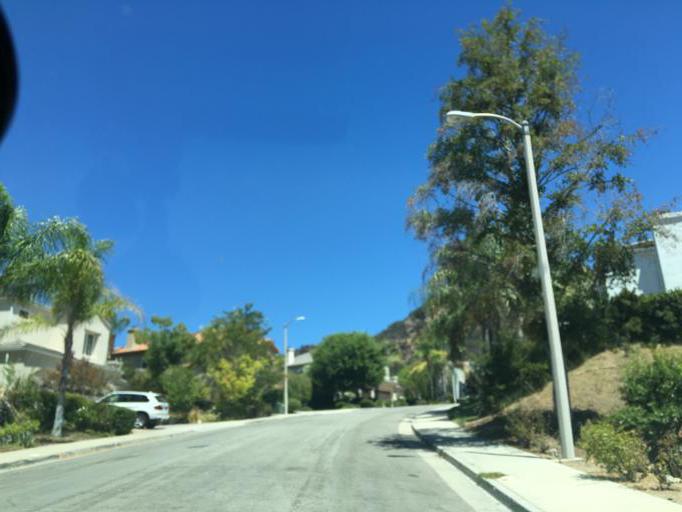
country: US
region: California
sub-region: Los Angeles County
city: Agoura Hills
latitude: 34.1167
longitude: -118.7768
